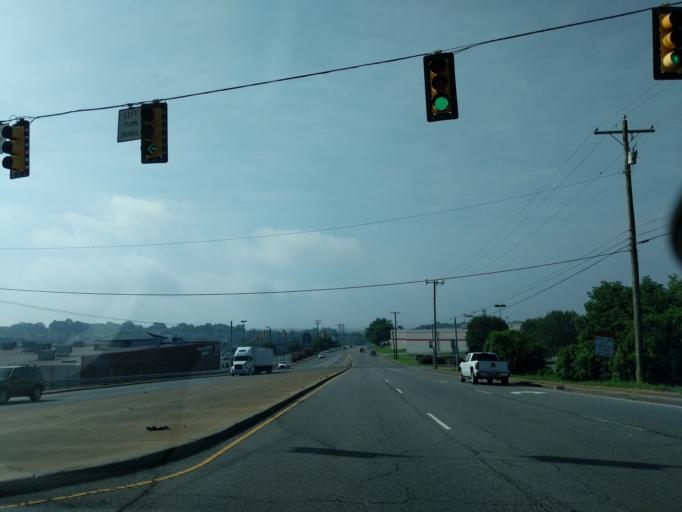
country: US
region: Tennessee
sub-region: Davidson County
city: Goodlettsville
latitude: 36.3069
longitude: -86.6945
